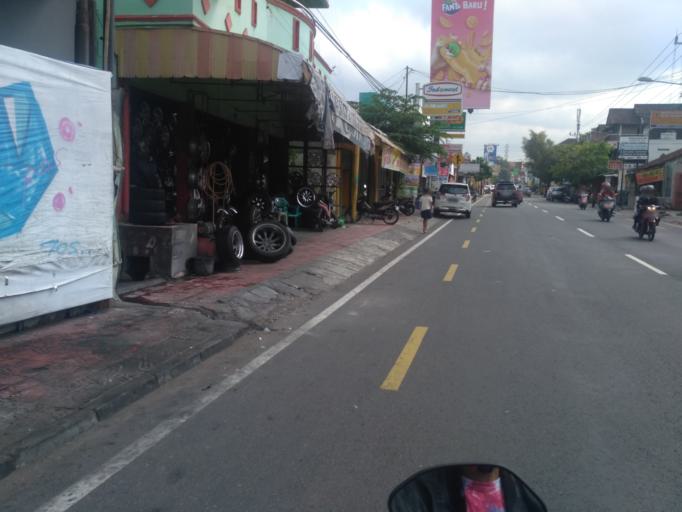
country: ID
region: Daerah Istimewa Yogyakarta
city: Melati
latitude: -7.7572
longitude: 110.3698
